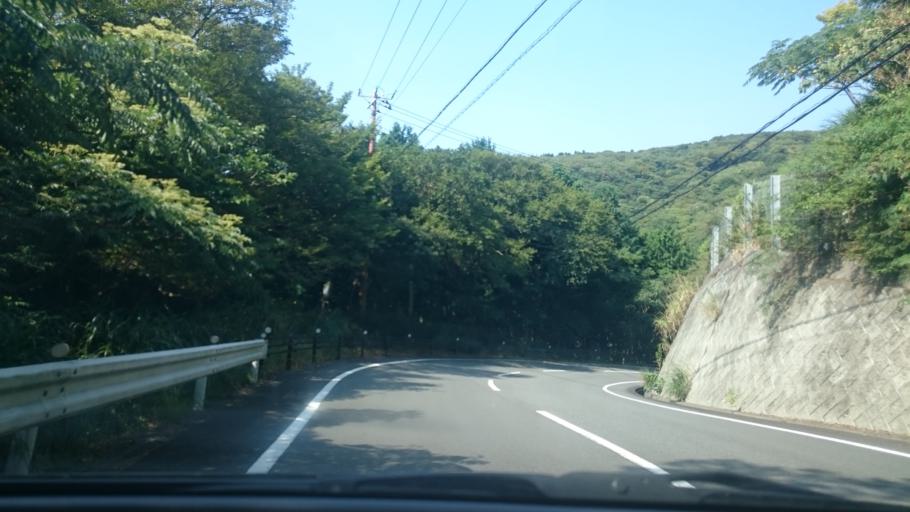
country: JP
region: Shizuoka
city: Heda
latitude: 34.9559
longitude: 138.7694
